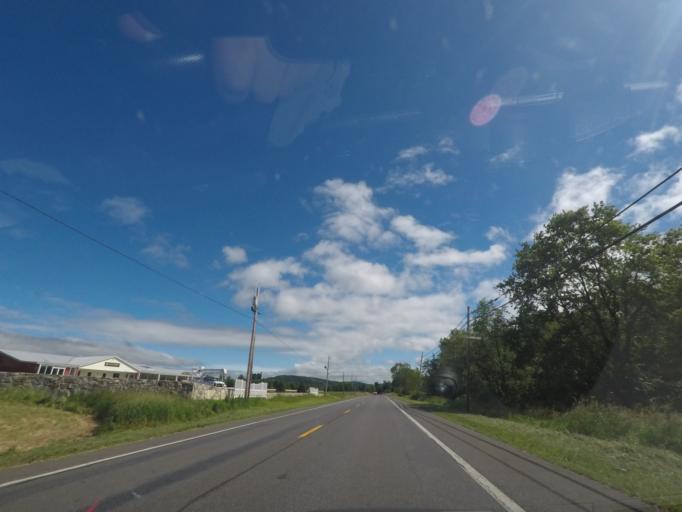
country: US
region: New York
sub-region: Dutchess County
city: Pine Plains
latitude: 42.0877
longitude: -73.5440
